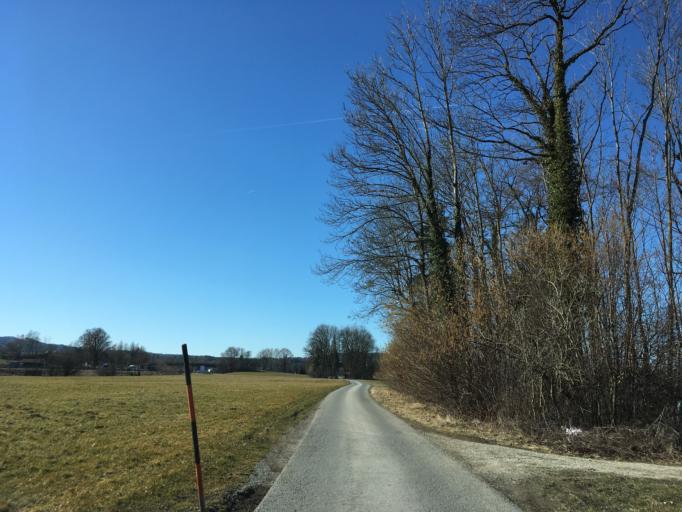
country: DE
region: Bavaria
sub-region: Upper Bavaria
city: Bad Aibling
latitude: 47.8229
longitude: 11.9924
